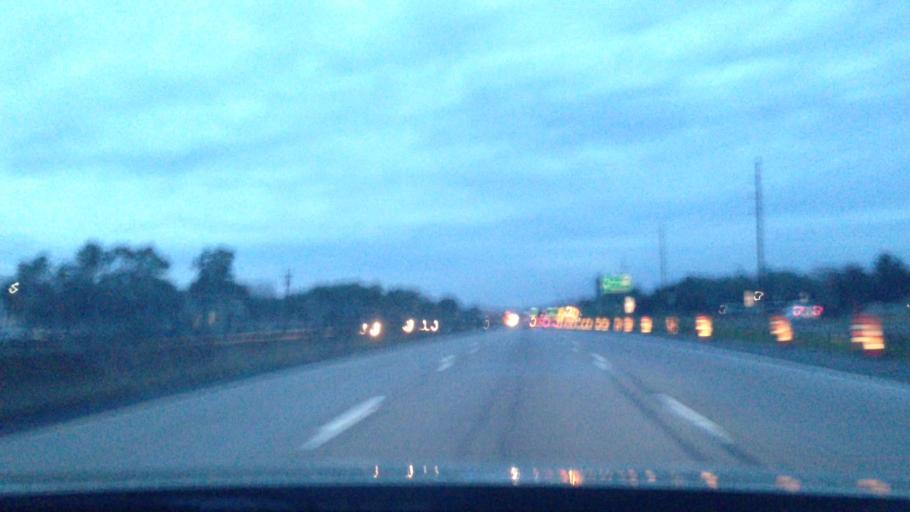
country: US
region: New York
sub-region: Suffolk County
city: North Bay Shore
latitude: 40.7336
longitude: -73.2580
